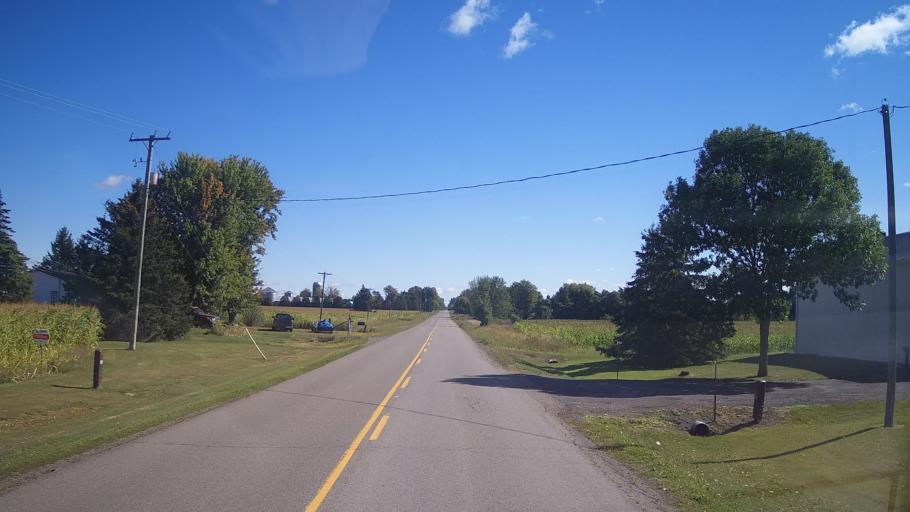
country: CA
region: Ontario
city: Prescott
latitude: 44.9154
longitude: -75.3667
